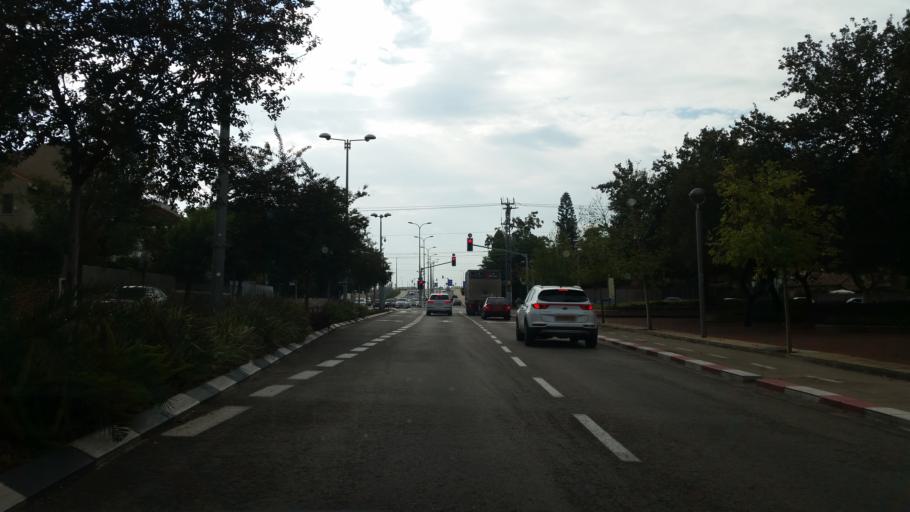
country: IL
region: Central District
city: Ra'anana
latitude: 32.1755
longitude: 34.8693
